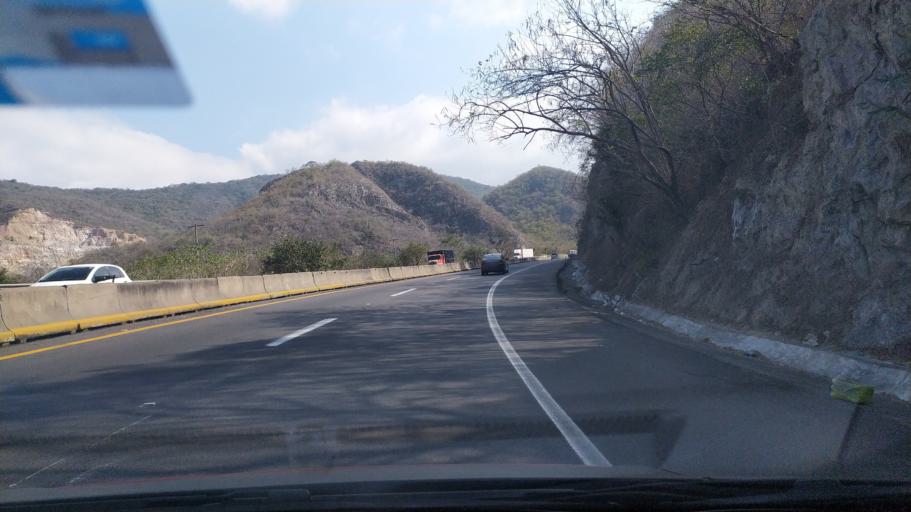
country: MX
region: Colima
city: Ixtlahuacan
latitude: 19.0810
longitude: -103.7748
